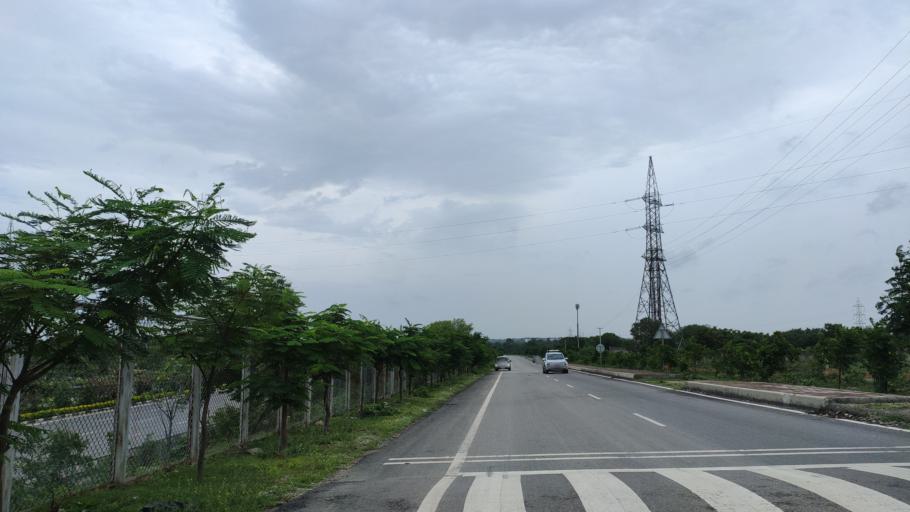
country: IN
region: Telangana
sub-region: Rangareddi
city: Secunderabad
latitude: 17.5776
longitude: 78.5985
